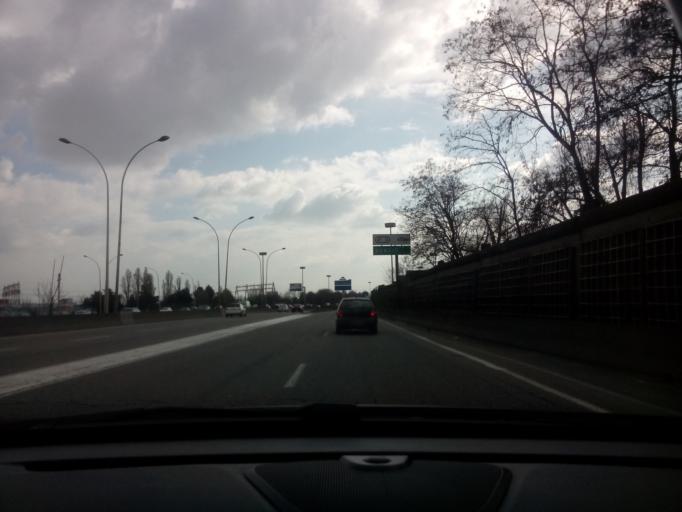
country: FR
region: Ile-de-France
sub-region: Departement du Val-de-Marne
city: Chevilly-Larue
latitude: 48.7727
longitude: 2.3453
